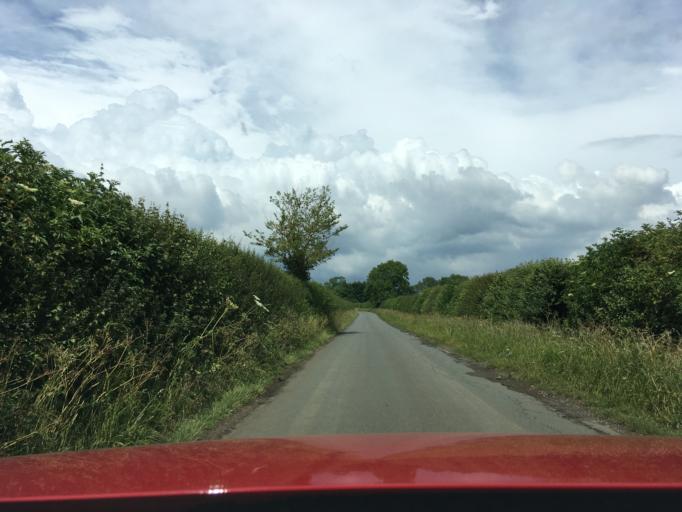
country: GB
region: England
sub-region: Gloucestershire
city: Chalford
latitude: 51.6897
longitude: -2.1296
